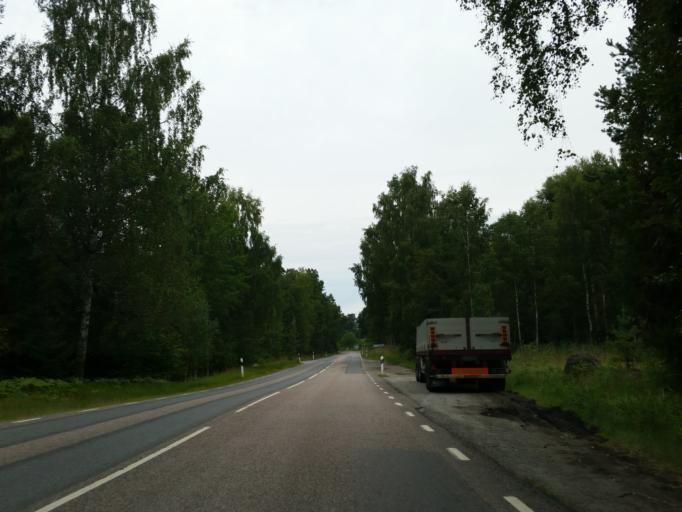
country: SE
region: Stockholm
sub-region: Sodertalje Kommun
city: Soedertaelje
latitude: 59.2003
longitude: 17.5727
